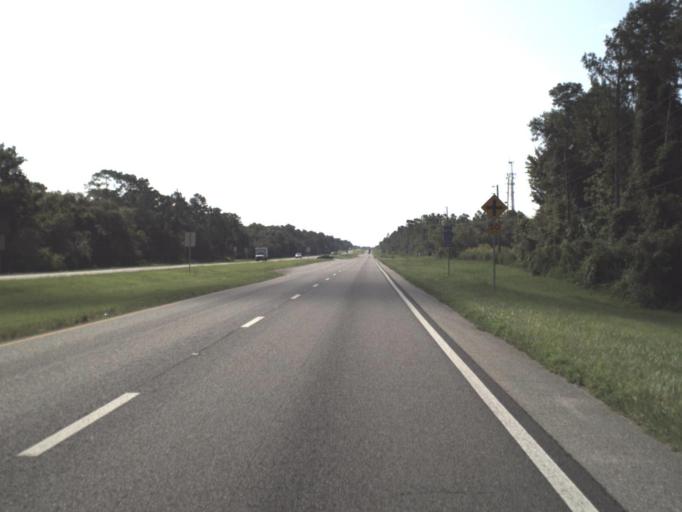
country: US
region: Florida
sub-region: Citrus County
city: Sugarmill Woods
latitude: 28.7207
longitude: -82.5493
